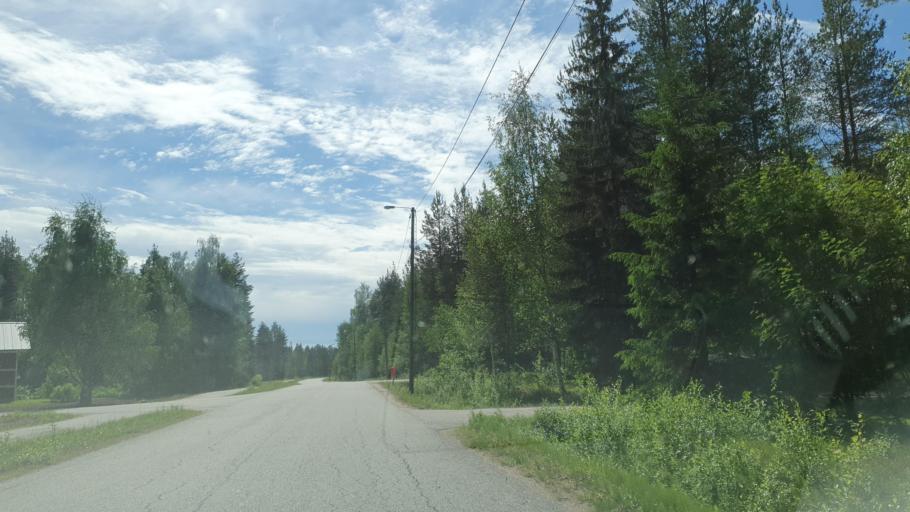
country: FI
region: Kainuu
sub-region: Kehys-Kainuu
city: Hyrynsalmi
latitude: 64.6901
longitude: 28.4701
